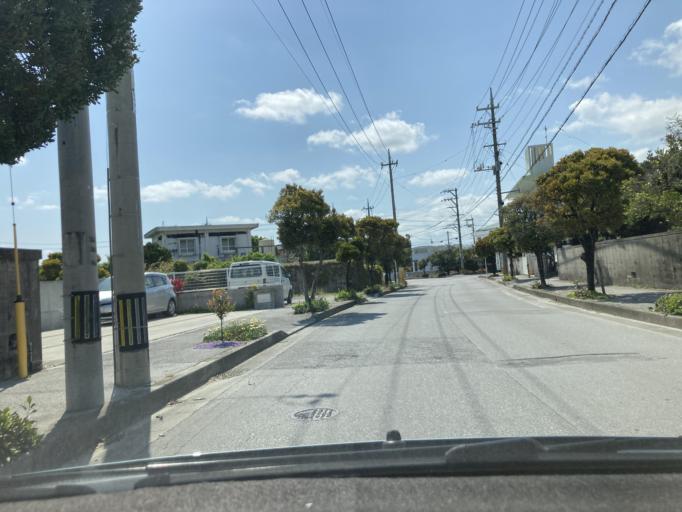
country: JP
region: Okinawa
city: Ginowan
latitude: 26.2608
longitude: 127.7913
